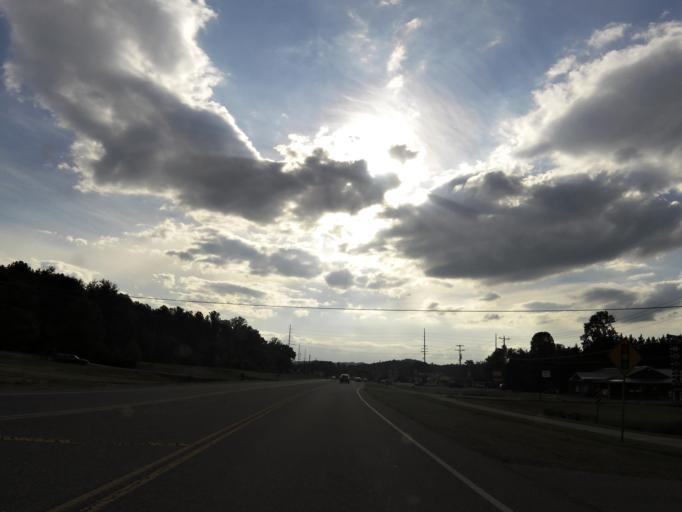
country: US
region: Tennessee
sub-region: Blount County
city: Wildwood
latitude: 35.6784
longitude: -83.7316
